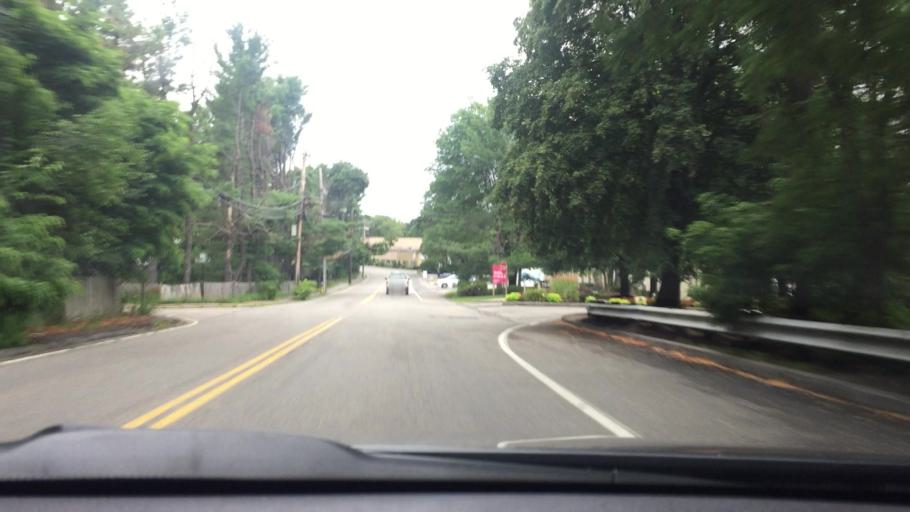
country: US
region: Massachusetts
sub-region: Norfolk County
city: Needham
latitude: 42.3039
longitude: -71.2298
